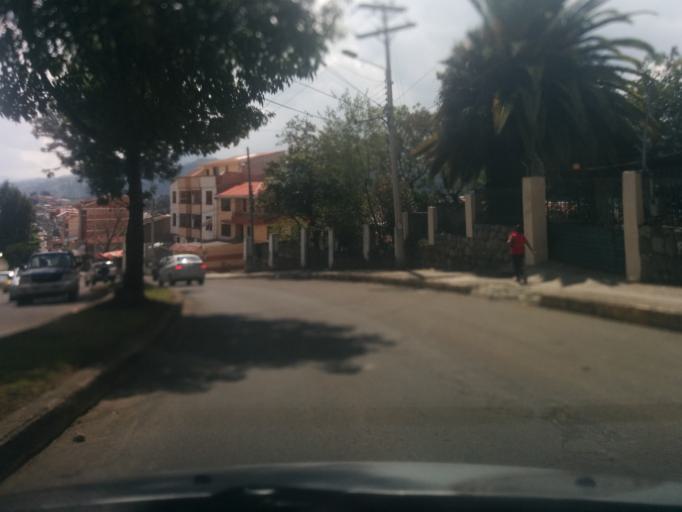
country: EC
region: Azuay
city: Cuenca
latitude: -2.9002
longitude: -78.9875
